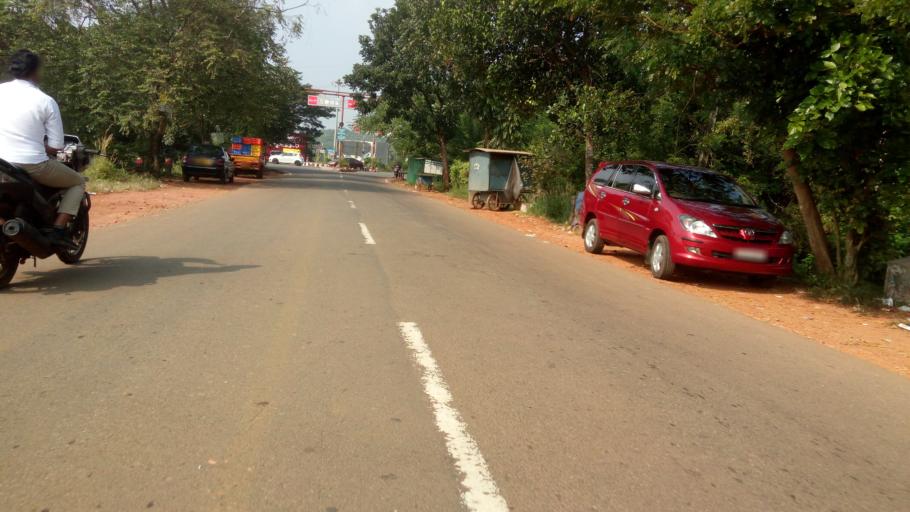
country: IN
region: Kerala
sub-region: Malappuram
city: Malappuram
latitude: 11.0030
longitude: 76.0143
